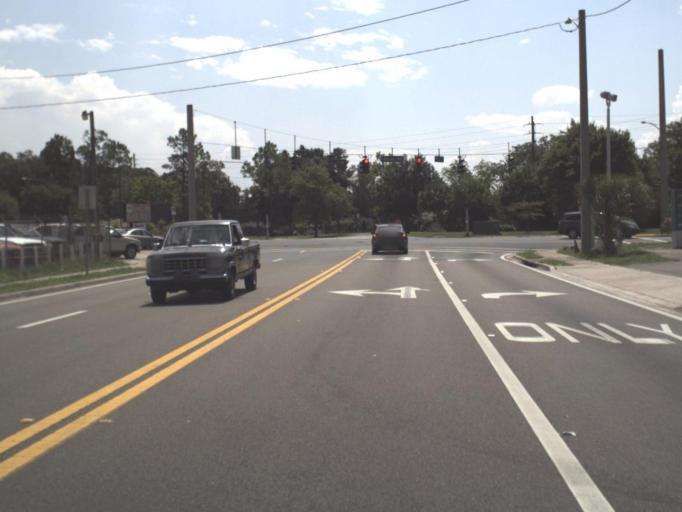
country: US
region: Florida
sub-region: Alachua County
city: Gainesville
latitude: 29.6738
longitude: -82.2976
